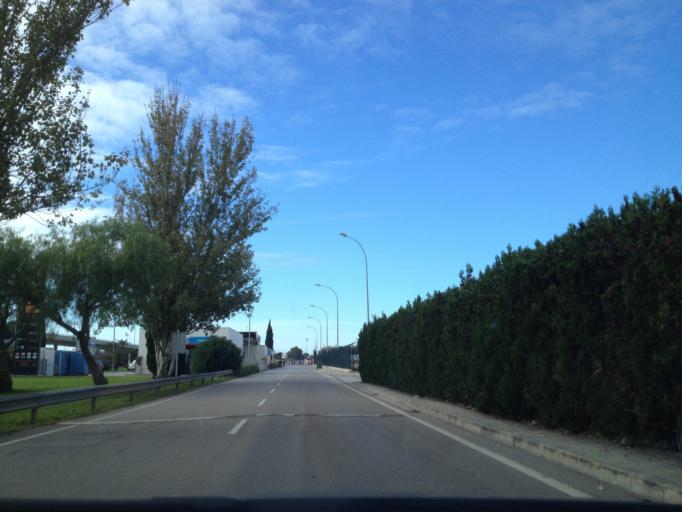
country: ES
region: Balearic Islands
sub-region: Illes Balears
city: s'Arenal
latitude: 39.5468
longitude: 2.7238
